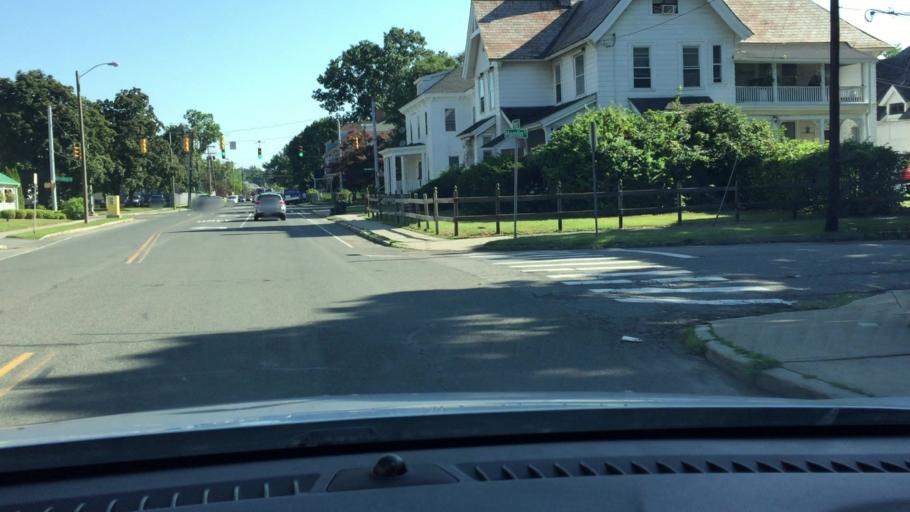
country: US
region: Massachusetts
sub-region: Berkshire County
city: Pittsfield
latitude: 42.4539
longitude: -73.2495
